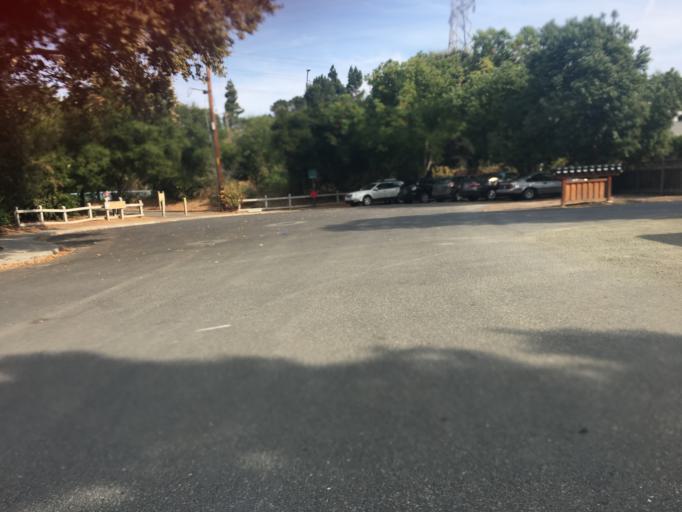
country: US
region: California
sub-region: Santa Clara County
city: Mountain View
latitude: 37.3951
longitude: -122.0702
